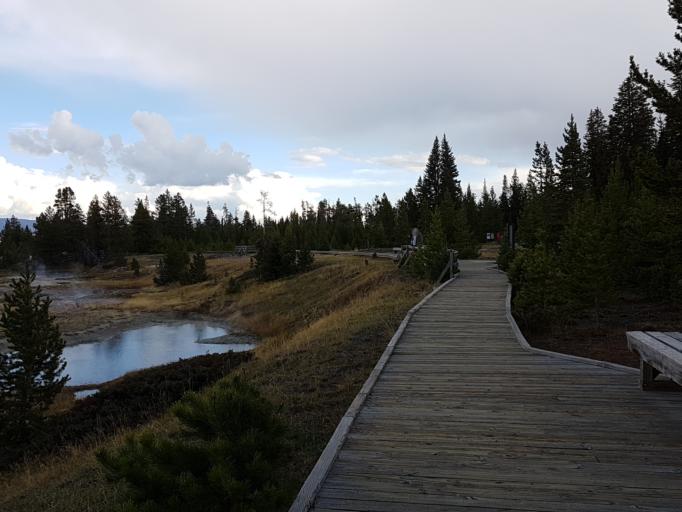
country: US
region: Montana
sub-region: Gallatin County
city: West Yellowstone
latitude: 44.4167
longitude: -110.5731
